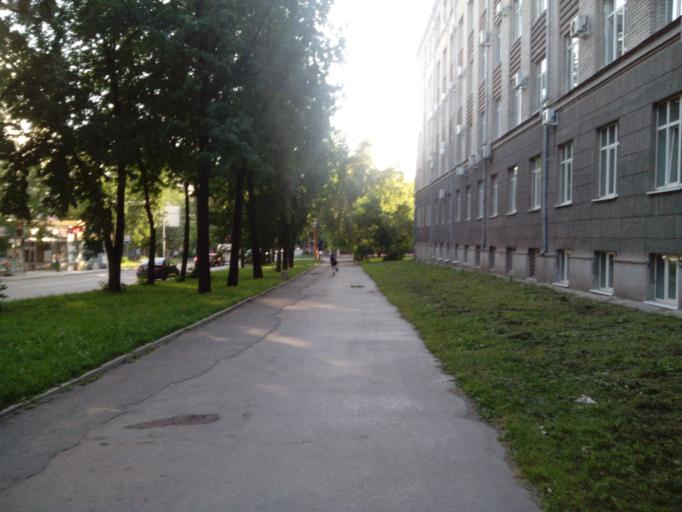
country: RU
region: Sverdlovsk
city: Yekaterinburg
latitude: 56.8476
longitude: 60.6558
